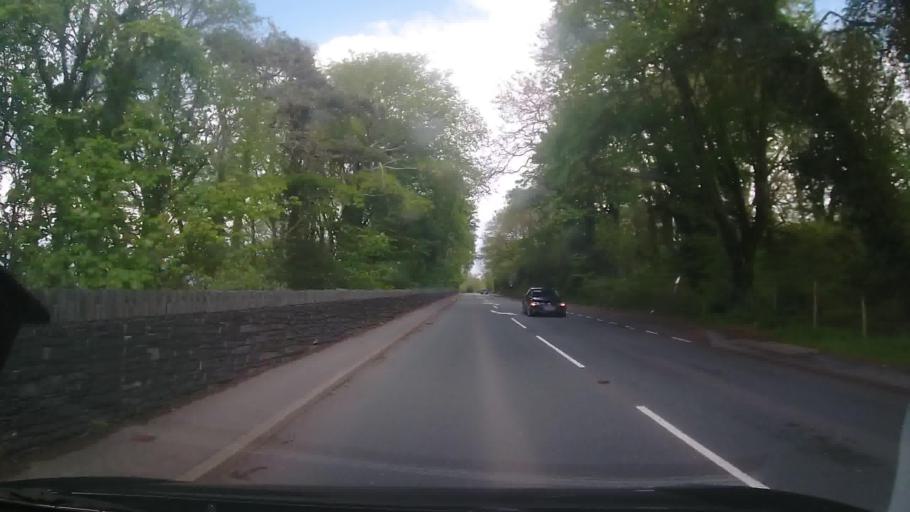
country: GB
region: Wales
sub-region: Gwynedd
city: Porthmadog
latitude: 52.9234
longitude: -4.0987
